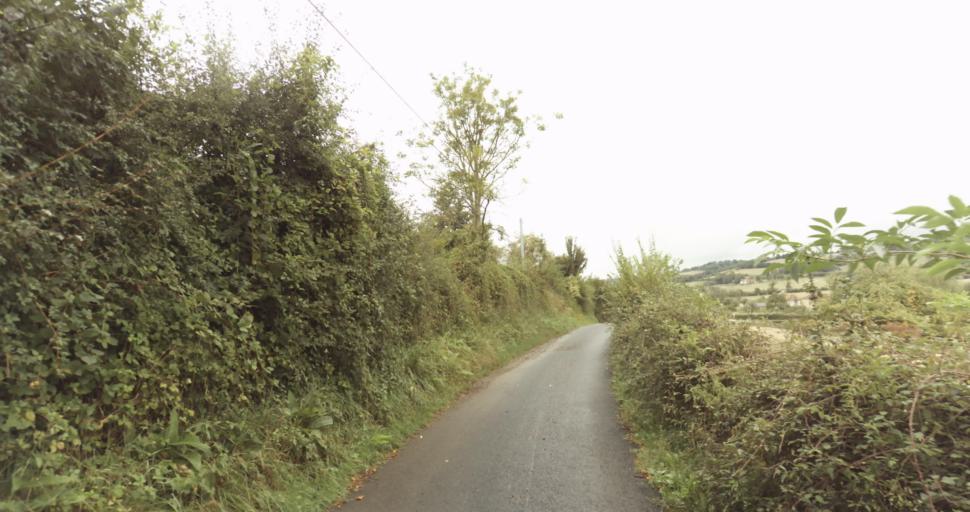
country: FR
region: Lower Normandy
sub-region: Departement de l'Orne
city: Vimoutiers
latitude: 48.8738
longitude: 0.2193
